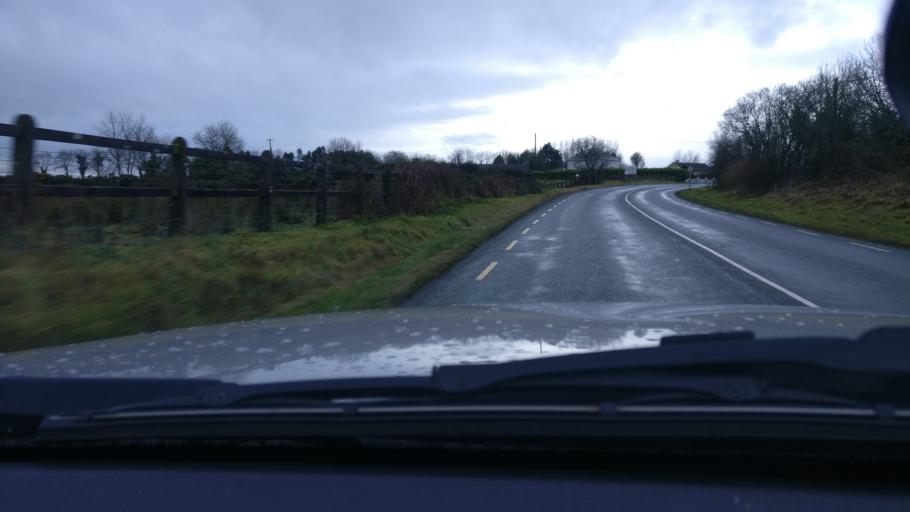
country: IE
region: Leinster
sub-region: An Longfort
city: Granard
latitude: 53.7790
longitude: -7.4712
